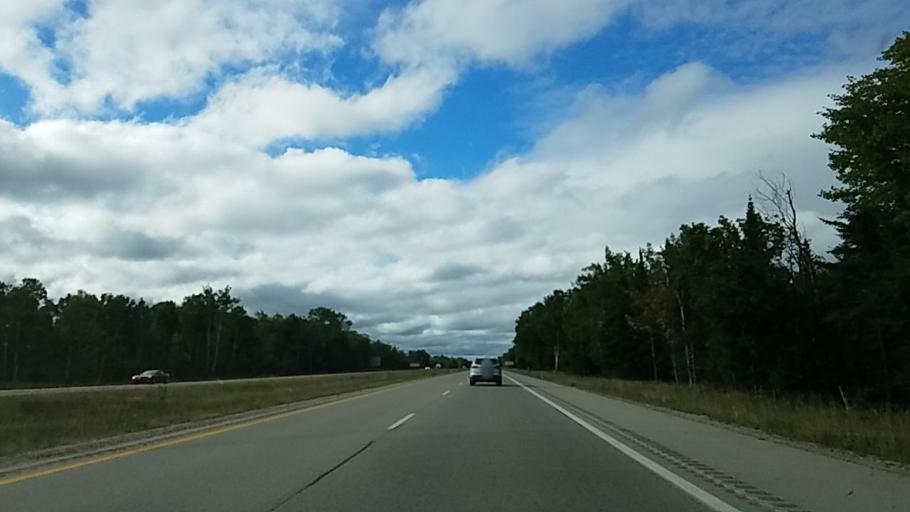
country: US
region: Michigan
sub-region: Mackinac County
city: Saint Ignace
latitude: 45.7490
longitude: -84.7289
